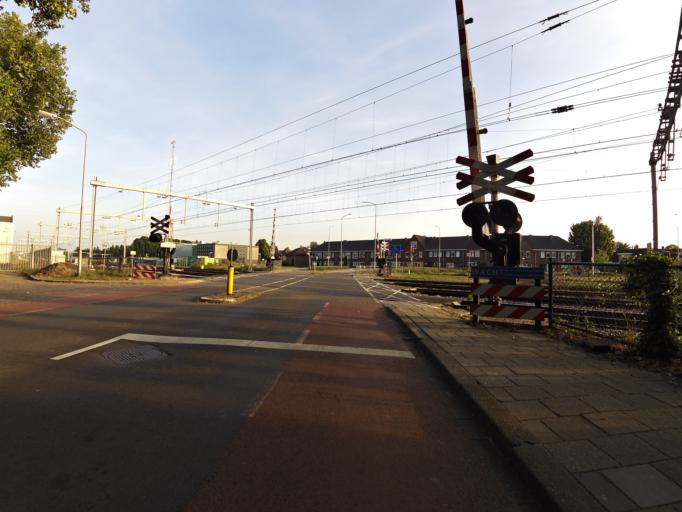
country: NL
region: Gelderland
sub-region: Gemeente Zevenaar
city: Zevenaar
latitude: 51.9227
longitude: 6.0748
